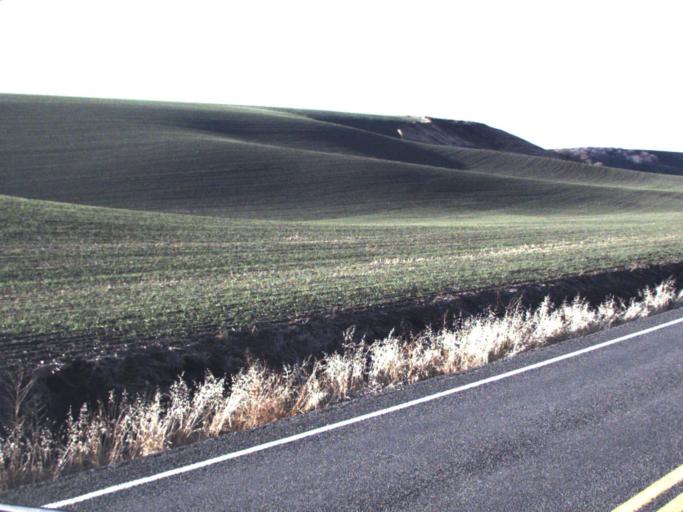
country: US
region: Washington
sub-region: Whitman County
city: Colfax
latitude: 46.7614
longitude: -117.4344
